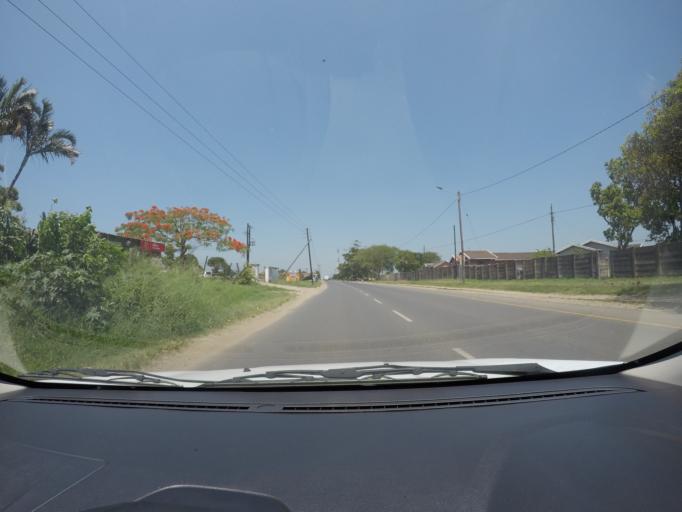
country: ZA
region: KwaZulu-Natal
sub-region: uThungulu District Municipality
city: eSikhawini
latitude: -28.8729
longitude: 31.9193
